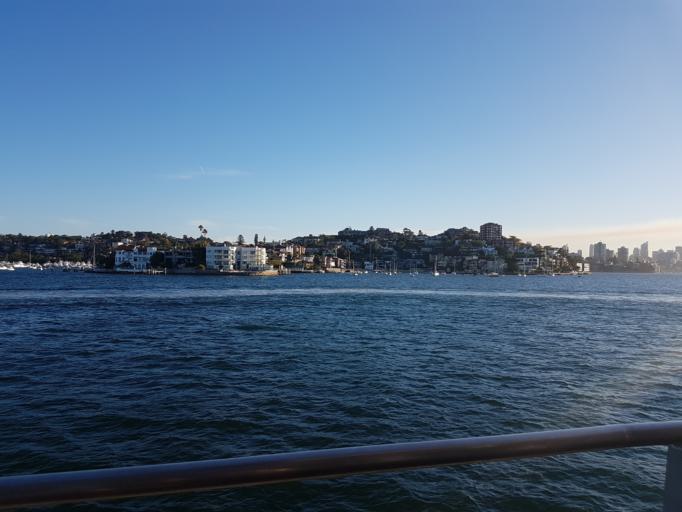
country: AU
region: New South Wales
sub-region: Woollahra
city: Point Piper
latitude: -33.8614
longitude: 151.2577
